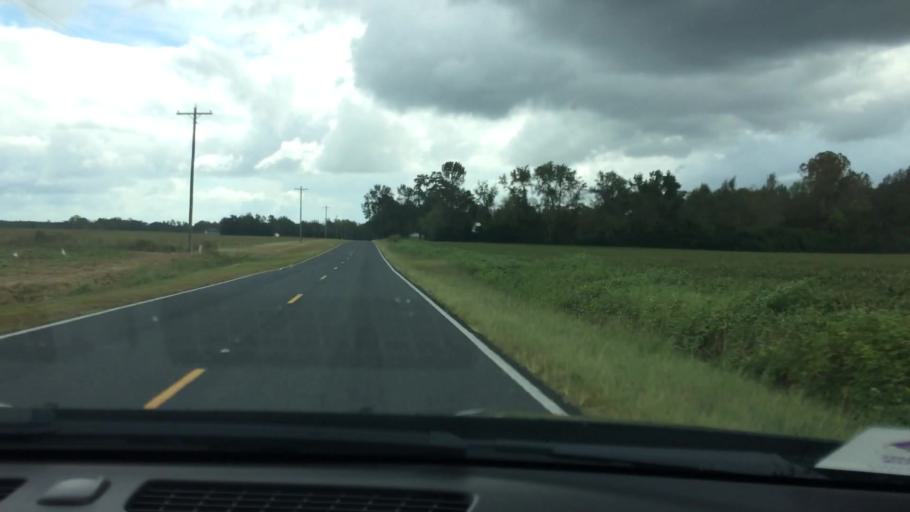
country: US
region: North Carolina
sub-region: Greene County
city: Maury
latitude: 35.5068
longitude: -77.5252
